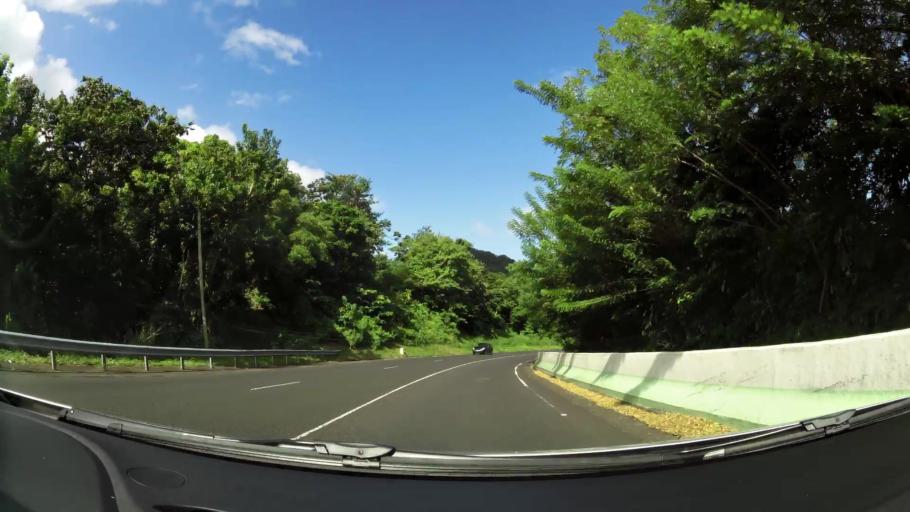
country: MQ
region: Martinique
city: Petite Riviere Salee
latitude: 14.7583
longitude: -60.9805
